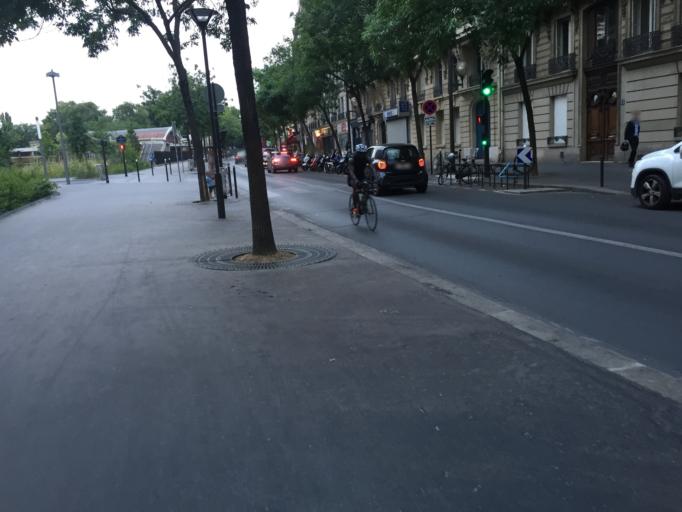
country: FR
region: Ile-de-France
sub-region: Departement des Hauts-de-Seine
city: Clichy
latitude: 48.8878
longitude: 2.3120
